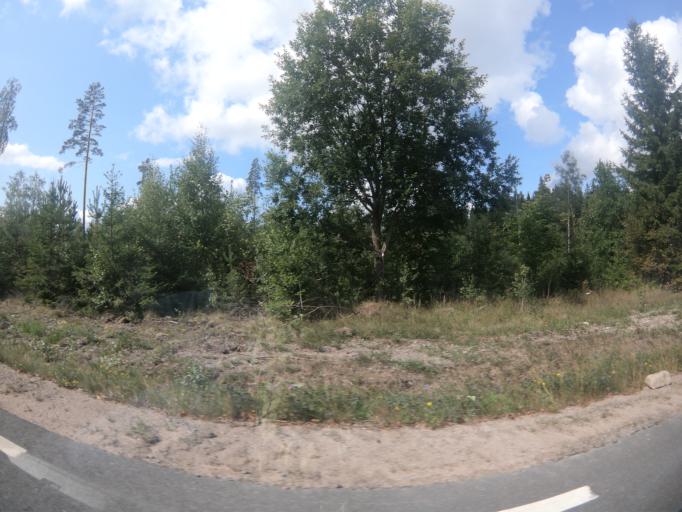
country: SE
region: Kronoberg
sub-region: Vaxjo Kommun
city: Braas
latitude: 57.1837
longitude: 14.9642
